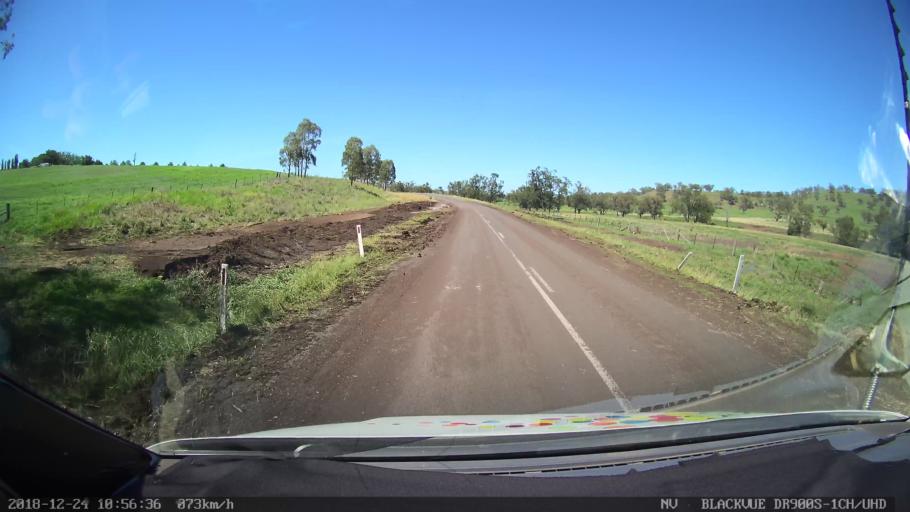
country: AU
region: New South Wales
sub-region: Upper Hunter Shire
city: Merriwa
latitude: -32.0273
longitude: 150.4174
